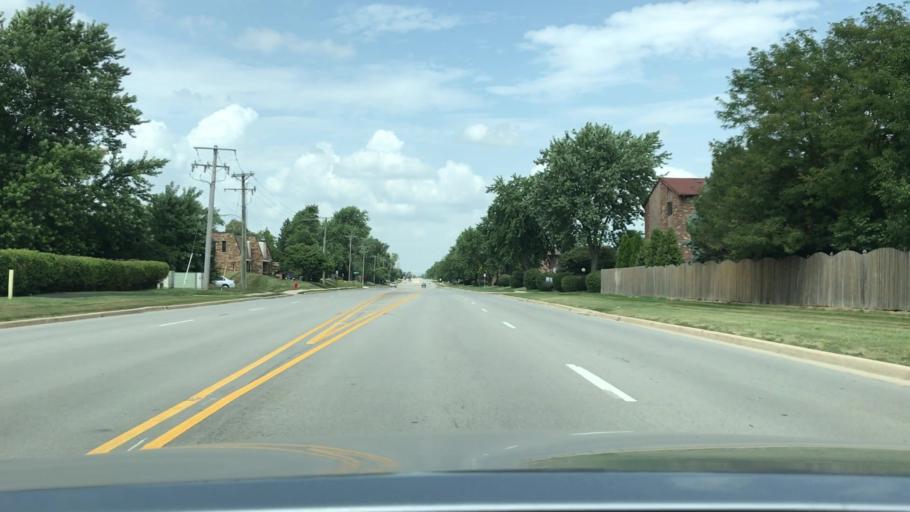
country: US
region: Illinois
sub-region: DuPage County
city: Woodridge
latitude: 41.7430
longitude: -88.0308
